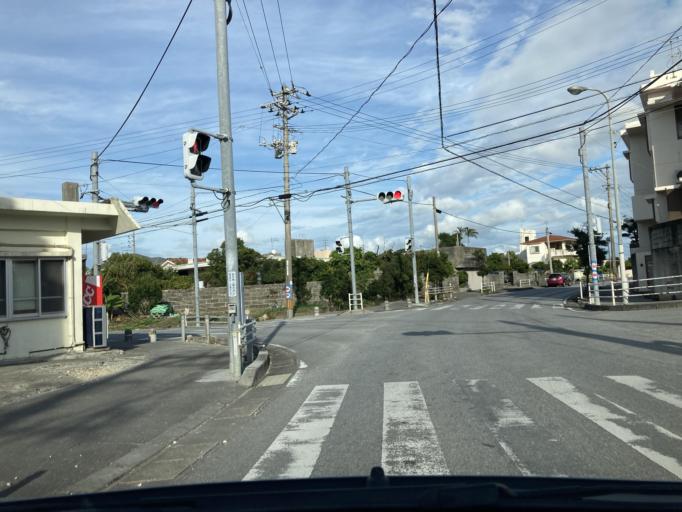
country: JP
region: Okinawa
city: Itoman
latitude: 26.1336
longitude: 127.7267
